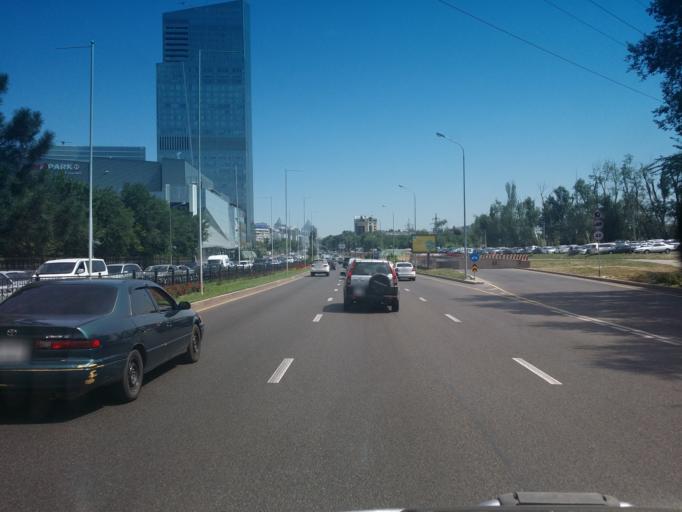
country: KZ
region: Almaty Qalasy
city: Almaty
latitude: 43.2162
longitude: 76.9259
